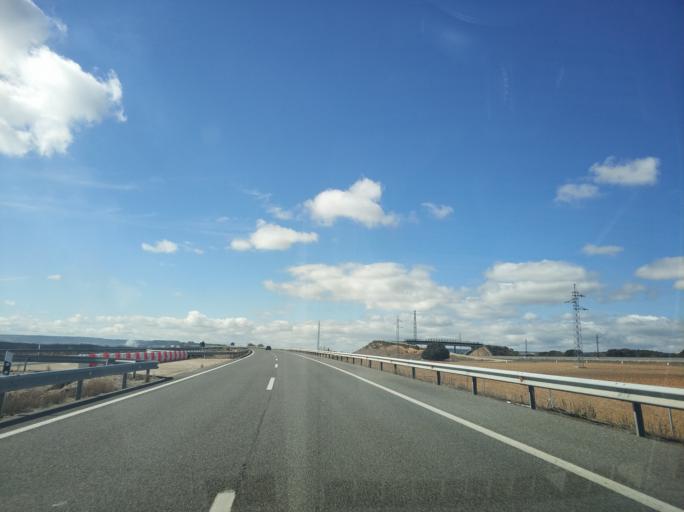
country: ES
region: Castille and Leon
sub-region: Provincia de Burgos
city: Villaverde-Mogina
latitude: 42.1700
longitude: -4.0705
